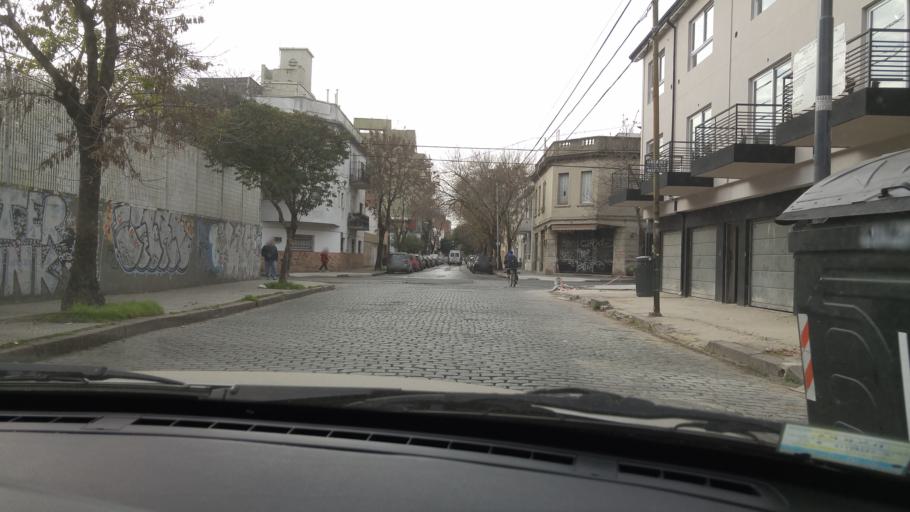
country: AR
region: Buenos Aires F.D.
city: Villa Santa Rita
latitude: -34.6280
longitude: -58.4877
